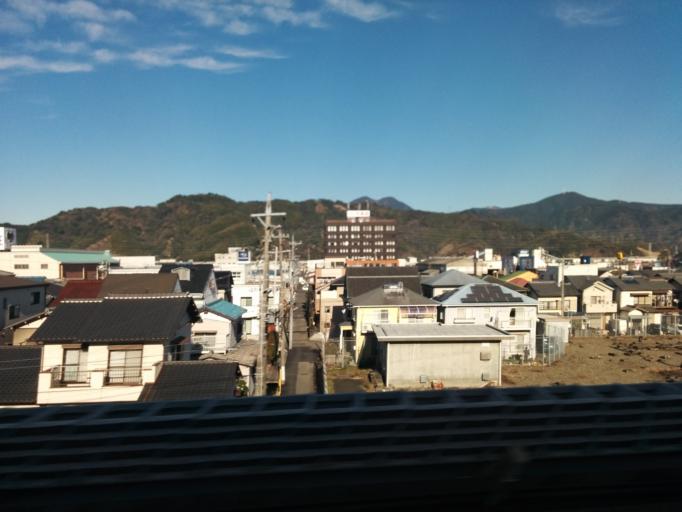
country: JP
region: Shizuoka
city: Shizuoka-shi
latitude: 35.0078
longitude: 138.4489
